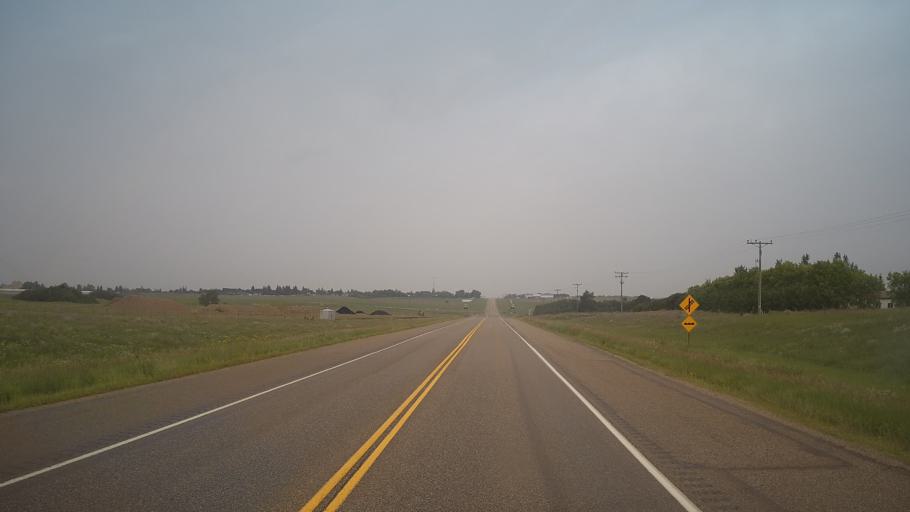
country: CA
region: Saskatchewan
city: Biggar
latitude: 52.0570
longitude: -107.9523
